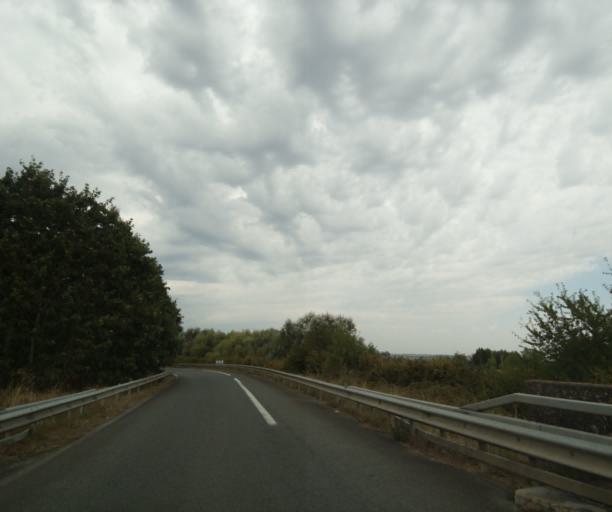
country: FR
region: Poitou-Charentes
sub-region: Departement de la Charente-Maritime
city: Tonnay-Charente
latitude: 45.9572
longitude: -0.8844
